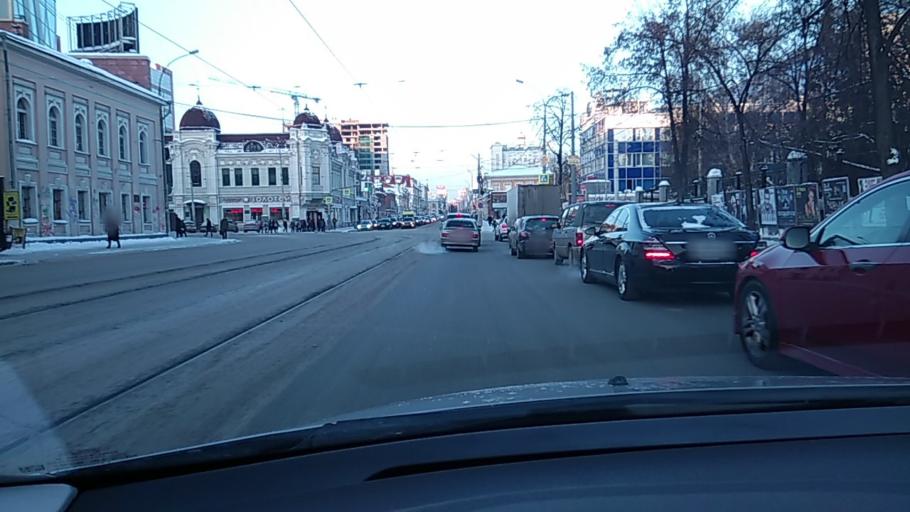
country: RU
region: Sverdlovsk
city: Yekaterinburg
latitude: 56.8301
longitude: 60.6013
